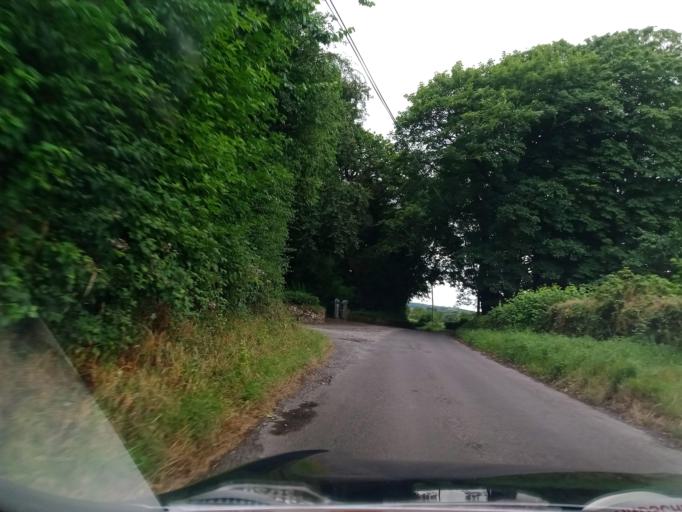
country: IE
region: Leinster
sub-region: Laois
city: Stradbally
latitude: 52.9901
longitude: -7.1744
